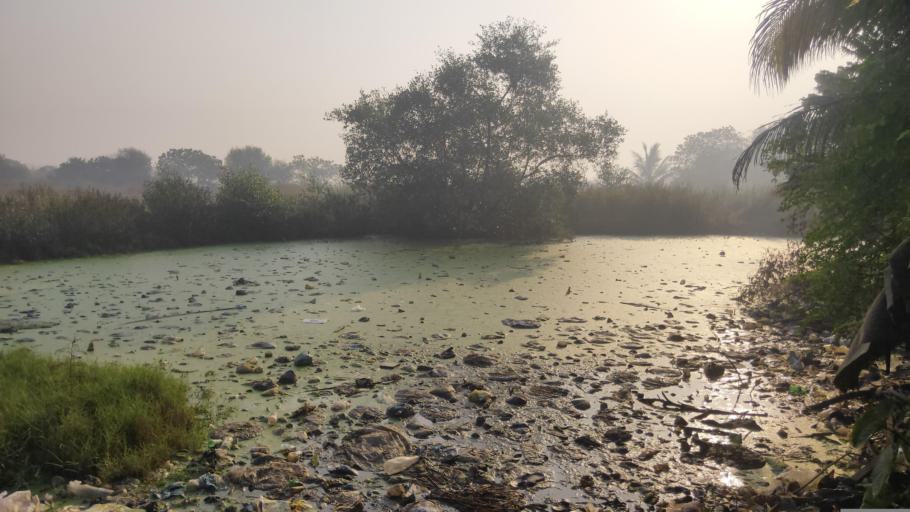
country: IN
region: Maharashtra
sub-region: Thane
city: Bhiwandi
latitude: 19.2739
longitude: 73.0073
